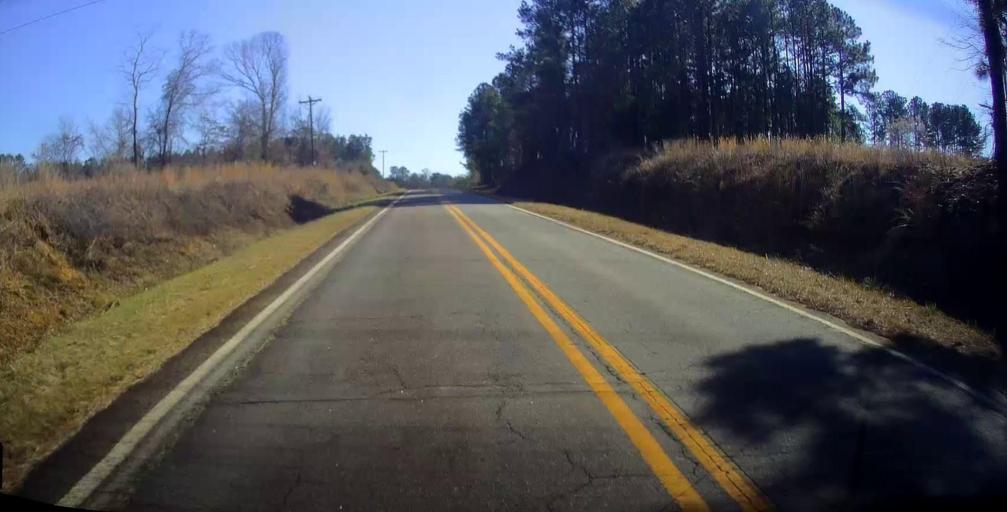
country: US
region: Georgia
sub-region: Crawford County
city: Knoxville
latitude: 32.6254
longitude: -83.9892
